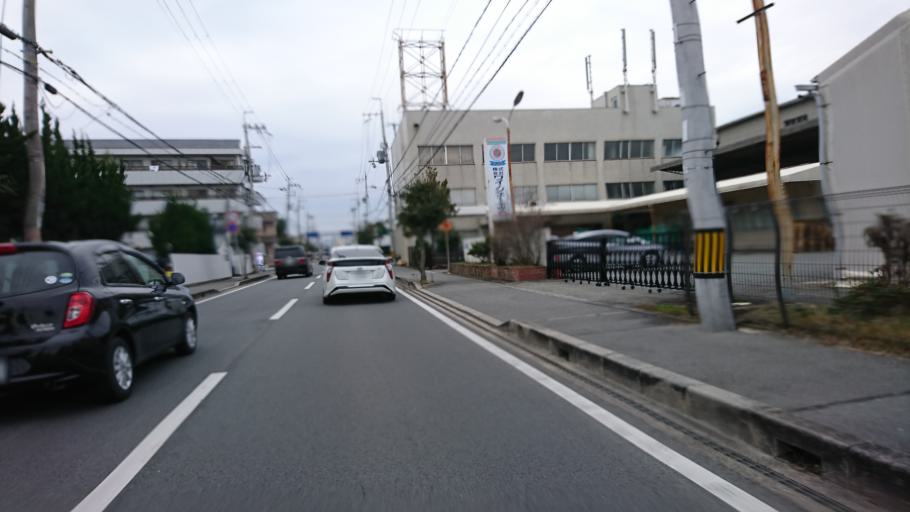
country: JP
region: Hyogo
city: Kakogawacho-honmachi
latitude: 34.7675
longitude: 134.8258
